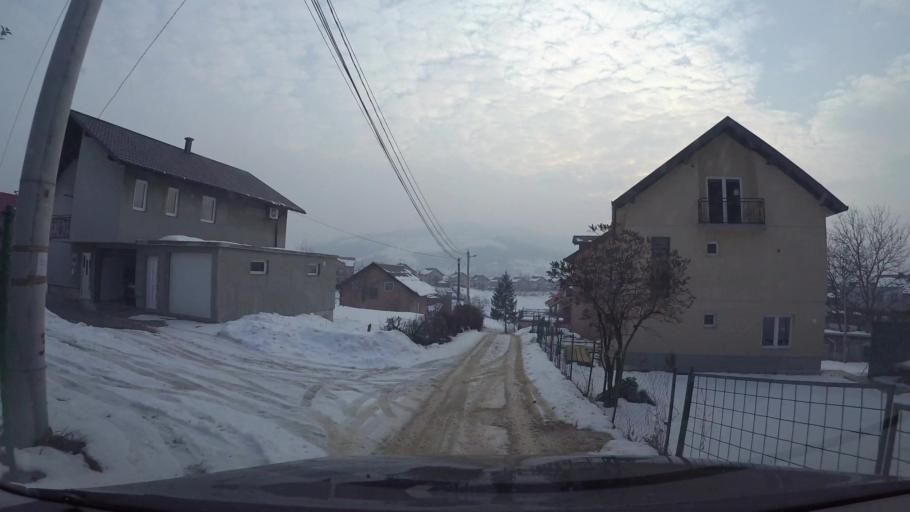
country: BA
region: Federation of Bosnia and Herzegovina
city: Hotonj
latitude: 43.8974
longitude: 18.3789
